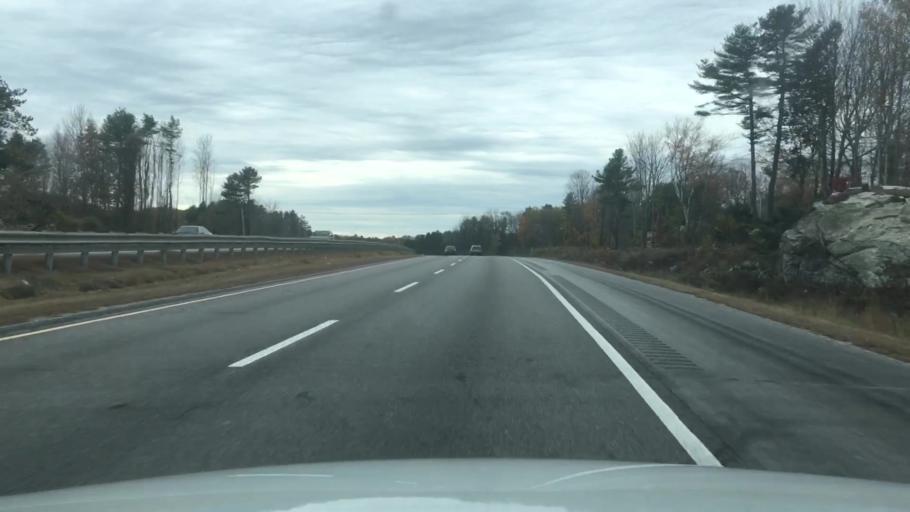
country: US
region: Maine
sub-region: Cumberland County
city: Freeport
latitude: 43.8687
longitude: -70.1030
